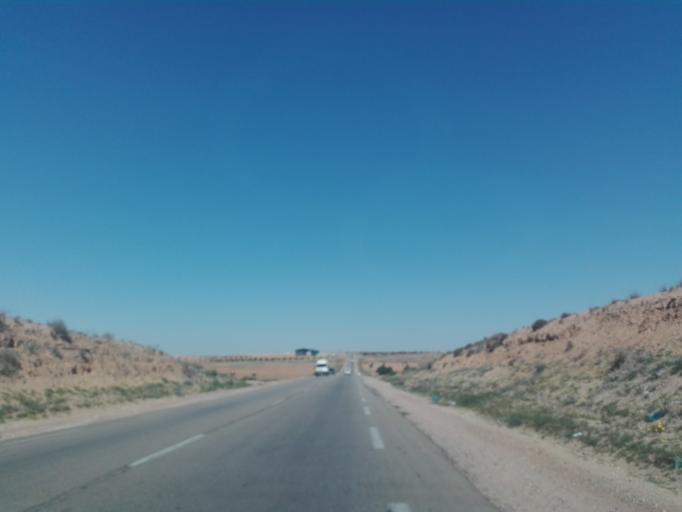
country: TN
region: Safaqis
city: Bi'r `Ali Bin Khalifah
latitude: 34.7317
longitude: 10.4236
